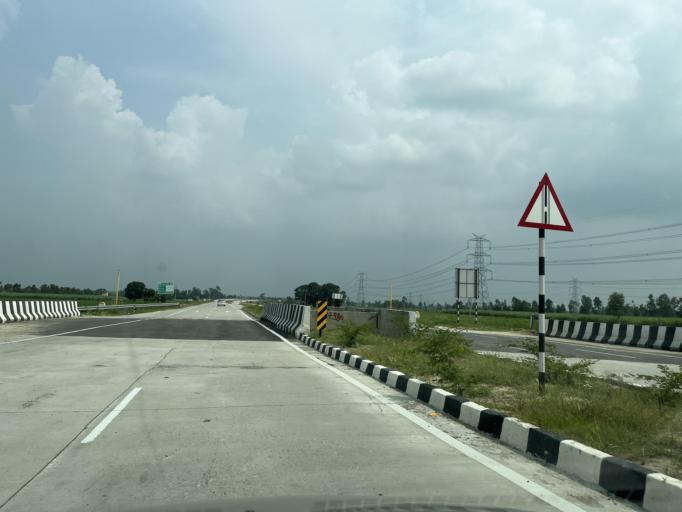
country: IN
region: Uttarakhand
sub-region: Udham Singh Nagar
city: Jaspur
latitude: 29.2926
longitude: 78.8474
